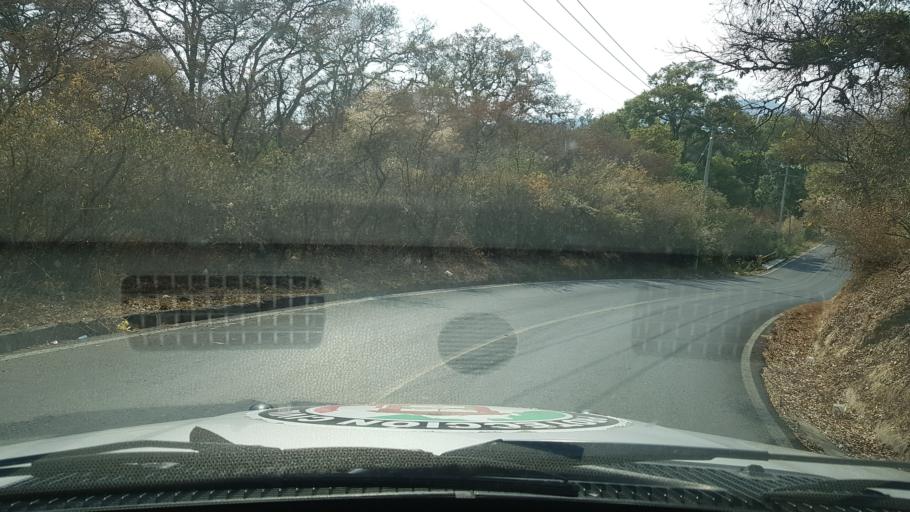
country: MX
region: Mexico
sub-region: Ozumba
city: San Jose Tlacotitlan
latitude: 18.9900
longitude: -98.8223
